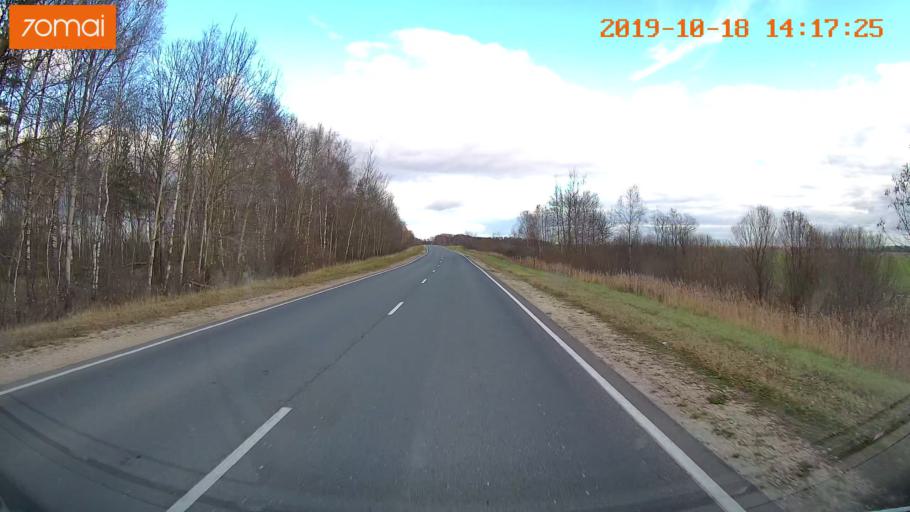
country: RU
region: Rjazan
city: Tuma
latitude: 55.1396
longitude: 40.3700
